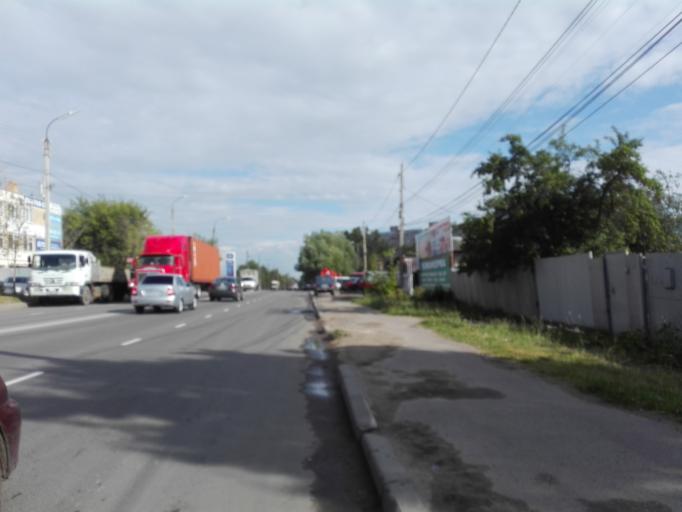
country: RU
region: Orjol
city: Orel
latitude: 52.9939
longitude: 36.1139
